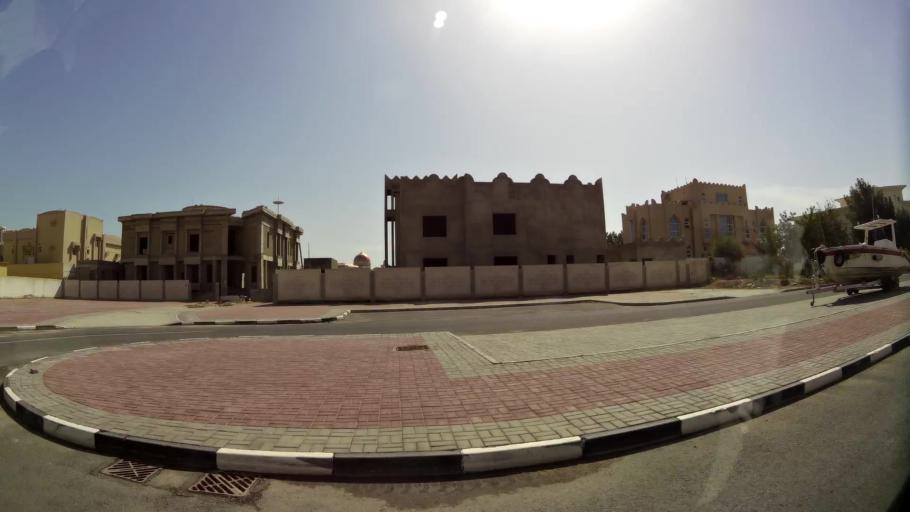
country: QA
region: Baladiyat ad Dawhah
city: Doha
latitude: 25.3610
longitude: 51.5192
